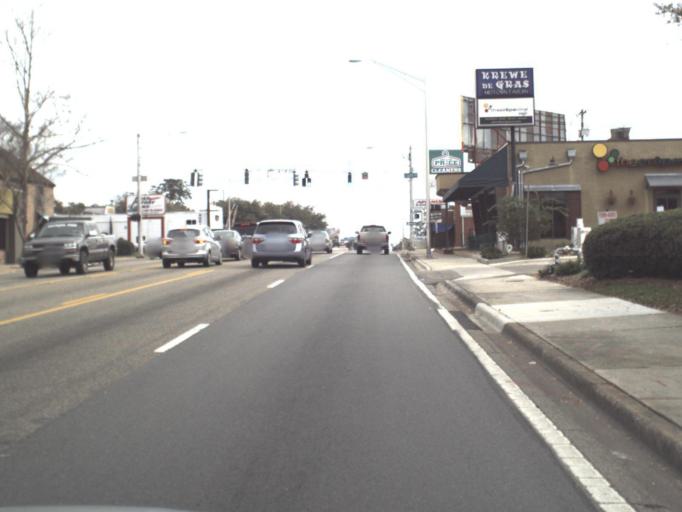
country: US
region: Florida
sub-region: Leon County
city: Tallahassee
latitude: 30.4571
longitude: -84.2808
